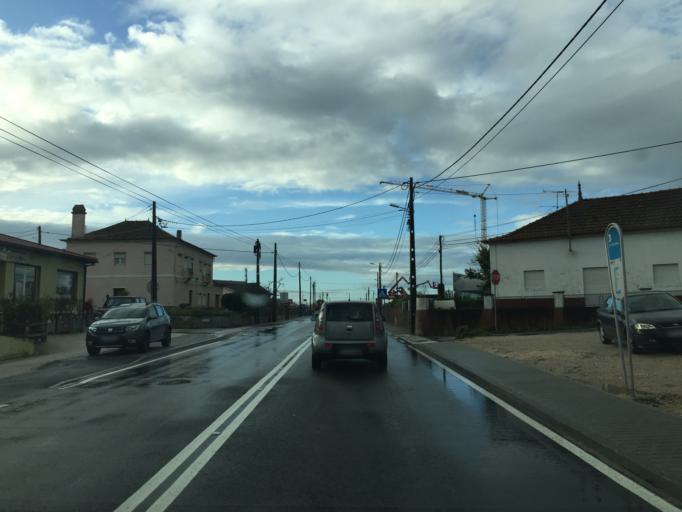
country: PT
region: Leiria
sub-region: Leiria
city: Amor
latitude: 39.7872
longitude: -8.8266
